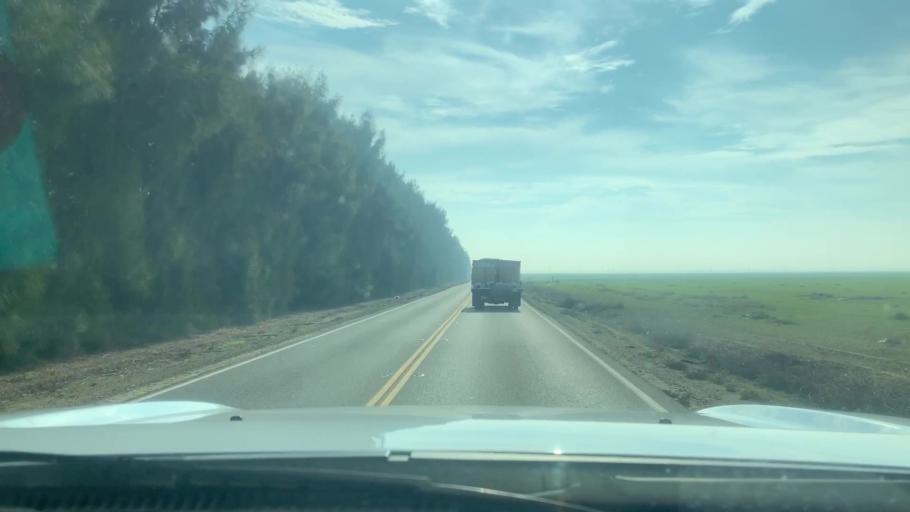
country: US
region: California
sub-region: Kern County
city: Lost Hills
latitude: 35.5148
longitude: -119.7512
